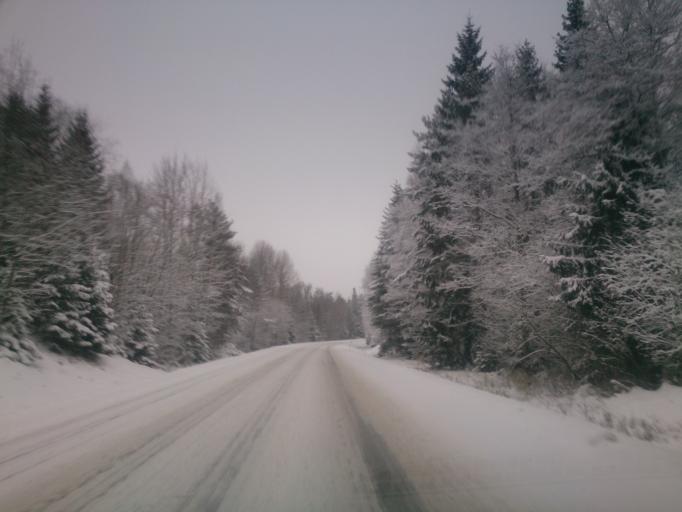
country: SE
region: OEstergoetland
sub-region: Finspangs Kommun
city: Finspang
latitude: 58.6152
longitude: 15.8111
